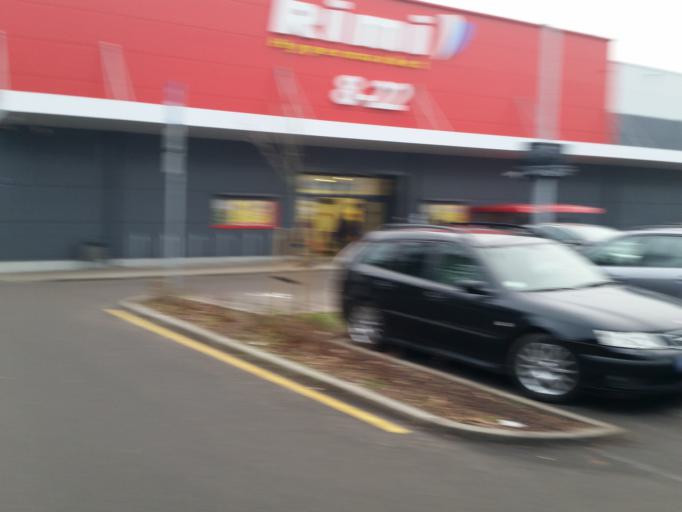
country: LV
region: Marupe
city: Marupe
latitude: 56.9448
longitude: 24.0112
